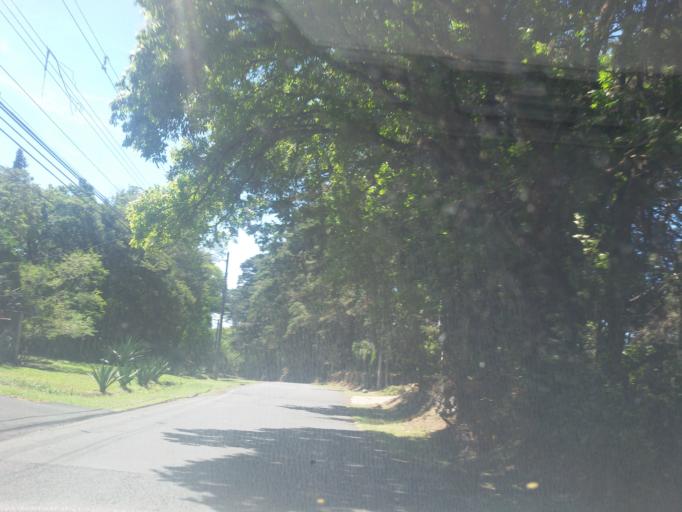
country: CR
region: Heredia
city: San Josecito
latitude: 10.0561
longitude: -84.0891
